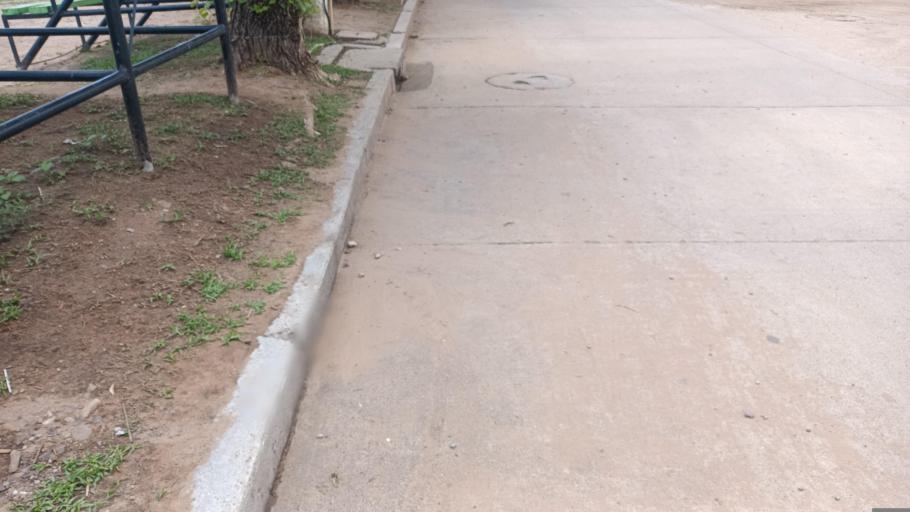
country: BO
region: Tarija
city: Entre Rios
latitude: -21.5297
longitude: -64.1729
